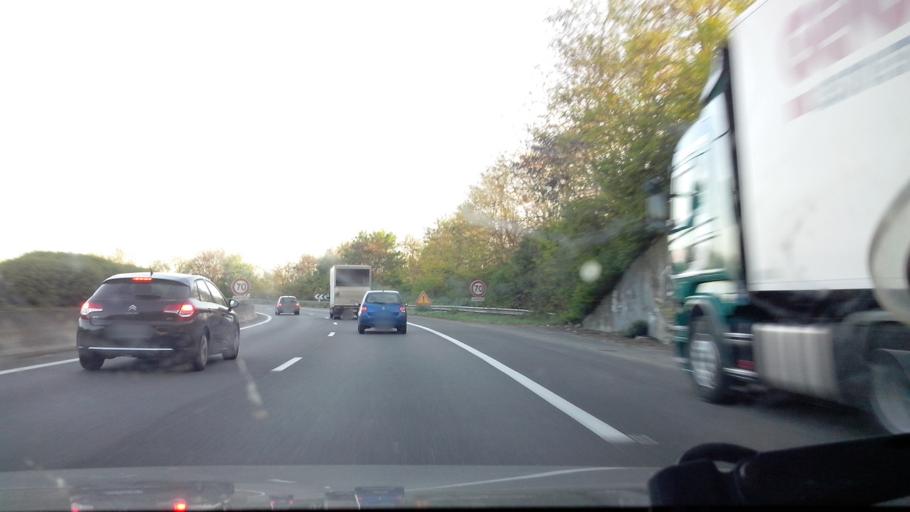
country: FR
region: Ile-de-France
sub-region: Departement de l'Essonne
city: Lisses
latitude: 48.6102
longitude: 2.4315
